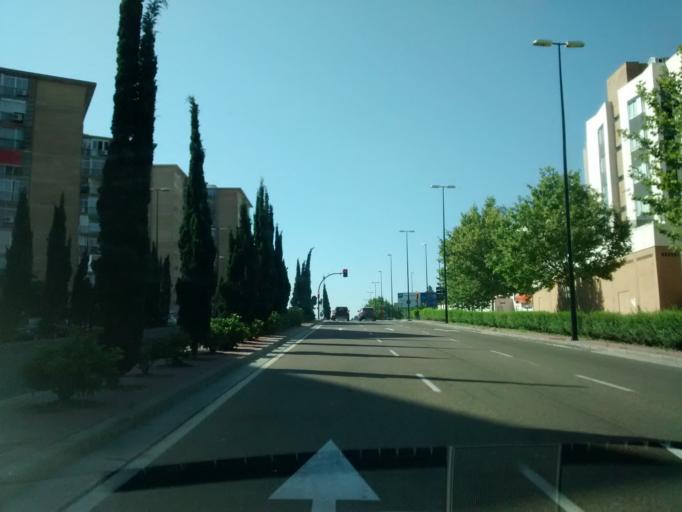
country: ES
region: Aragon
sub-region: Provincia de Zaragoza
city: Delicias
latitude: 41.6565
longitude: -0.9212
